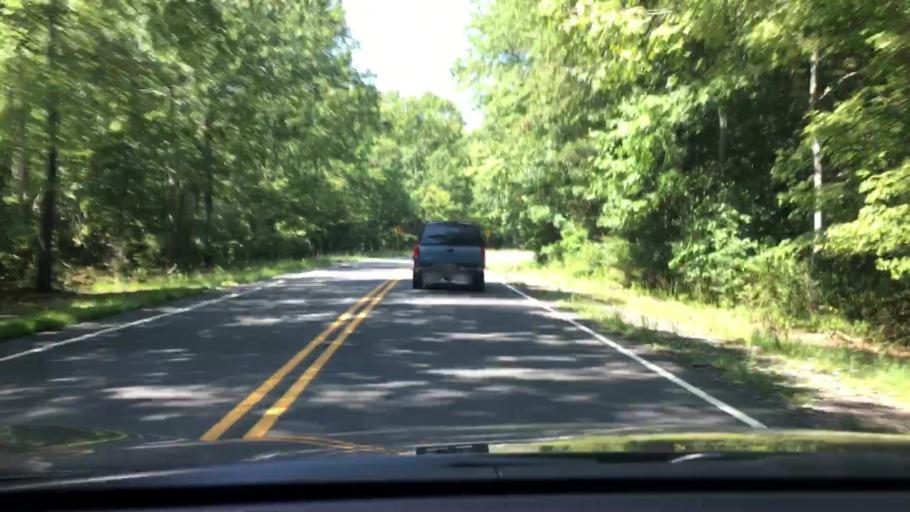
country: US
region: New Jersey
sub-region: Cape May County
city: Woodbine
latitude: 39.2590
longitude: -74.9091
